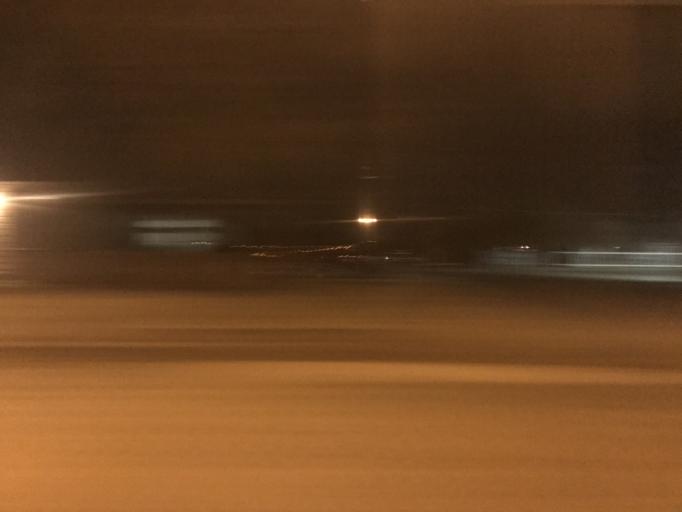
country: US
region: Texas
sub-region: Jones County
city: Anson
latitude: 32.7505
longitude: -99.8969
